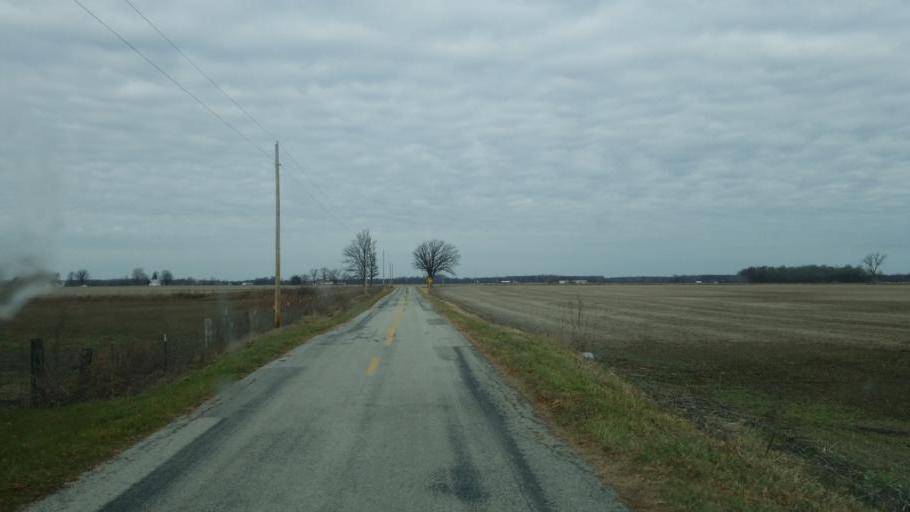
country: US
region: Ohio
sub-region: Union County
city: Richwood
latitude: 40.5435
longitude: -83.2906
